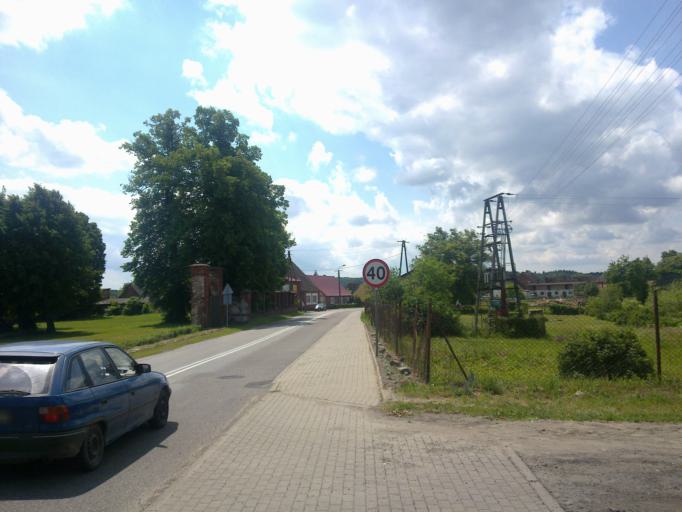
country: PL
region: West Pomeranian Voivodeship
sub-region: Powiat drawski
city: Wierzchowo
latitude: 53.5563
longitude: 16.1312
